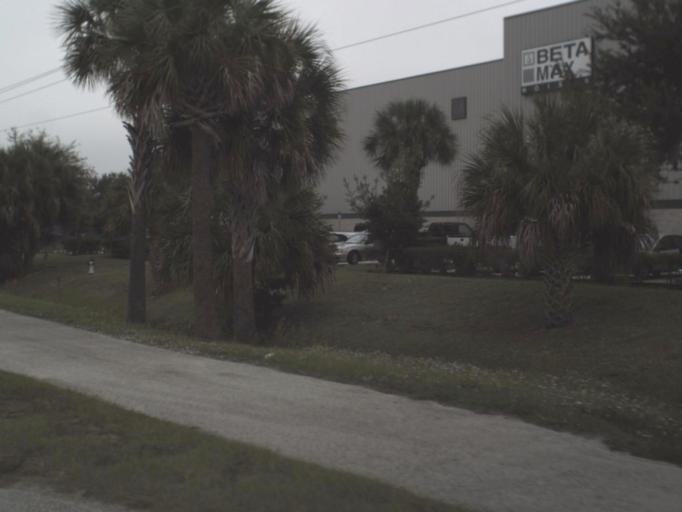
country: US
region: Florida
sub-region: Brevard County
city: Palm Bay
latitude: 28.0448
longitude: -80.5970
